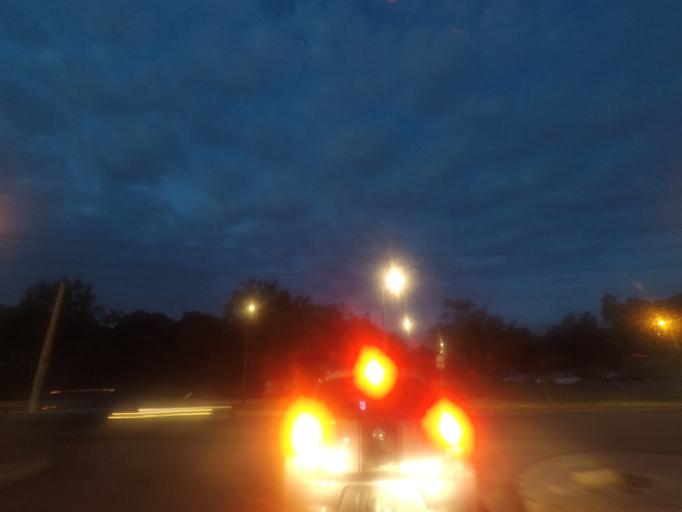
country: BR
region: Parana
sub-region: Pinhais
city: Pinhais
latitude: -25.3831
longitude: -49.2049
